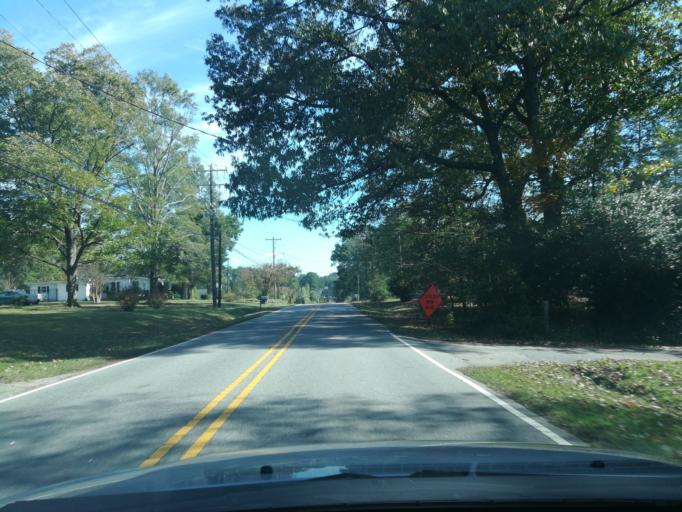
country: US
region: North Carolina
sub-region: Durham County
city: Durham
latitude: 35.9755
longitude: -78.9739
